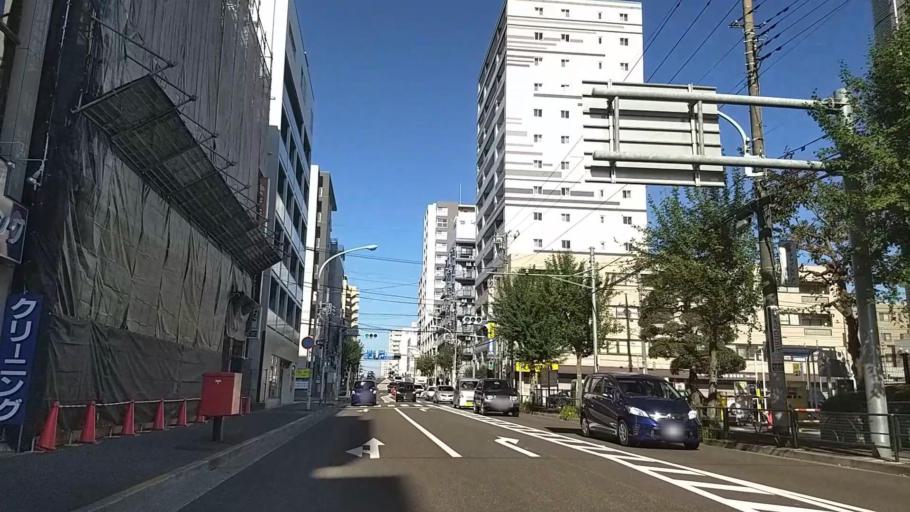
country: JP
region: Tokyo
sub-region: Machida-shi
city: Machida
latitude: 35.5459
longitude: 139.4498
